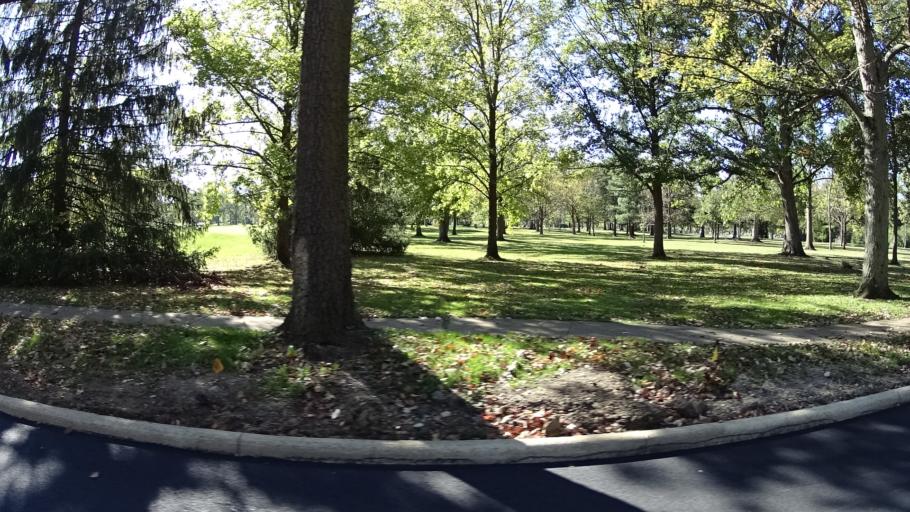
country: US
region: Ohio
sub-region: Lorain County
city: Oberlin
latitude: 41.2871
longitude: -82.2316
